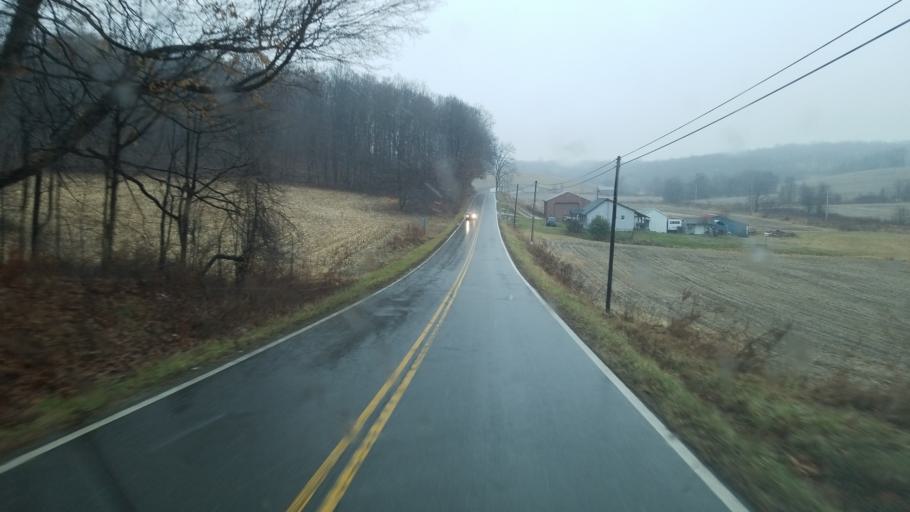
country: US
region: Ohio
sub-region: Licking County
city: Utica
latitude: 40.1870
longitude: -82.3376
